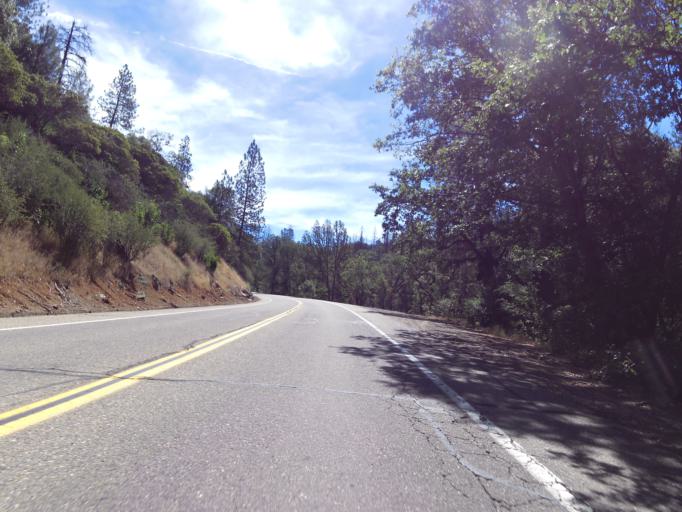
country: US
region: California
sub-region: Mariposa County
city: Midpines
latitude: 37.5195
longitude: -119.9466
